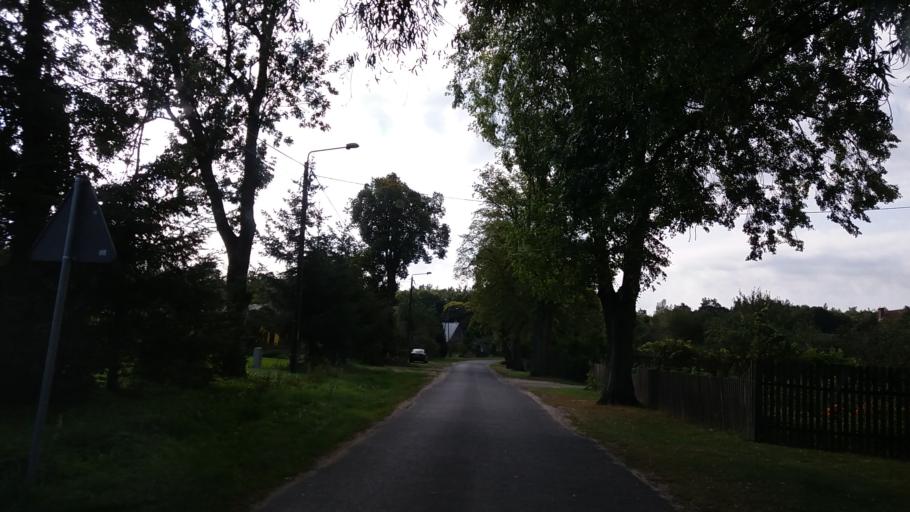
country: PL
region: West Pomeranian Voivodeship
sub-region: Powiat choszczenski
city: Choszczno
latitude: 53.2251
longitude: 15.3798
